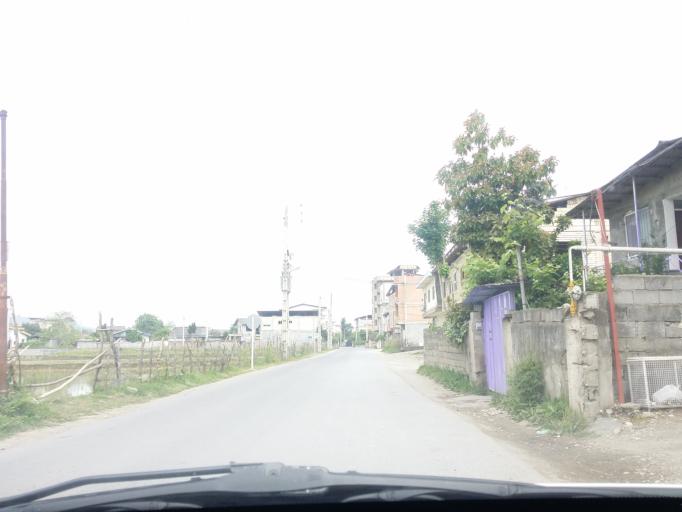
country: IR
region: Mazandaran
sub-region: Nowshahr
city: Nowshahr
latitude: 36.6256
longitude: 51.4901
